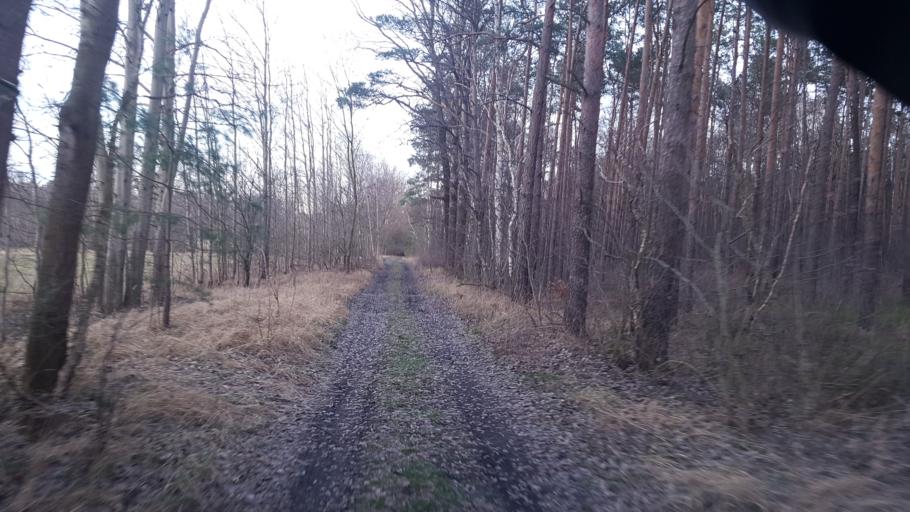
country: DE
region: Brandenburg
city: Schonborn
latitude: 51.5970
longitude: 13.4708
